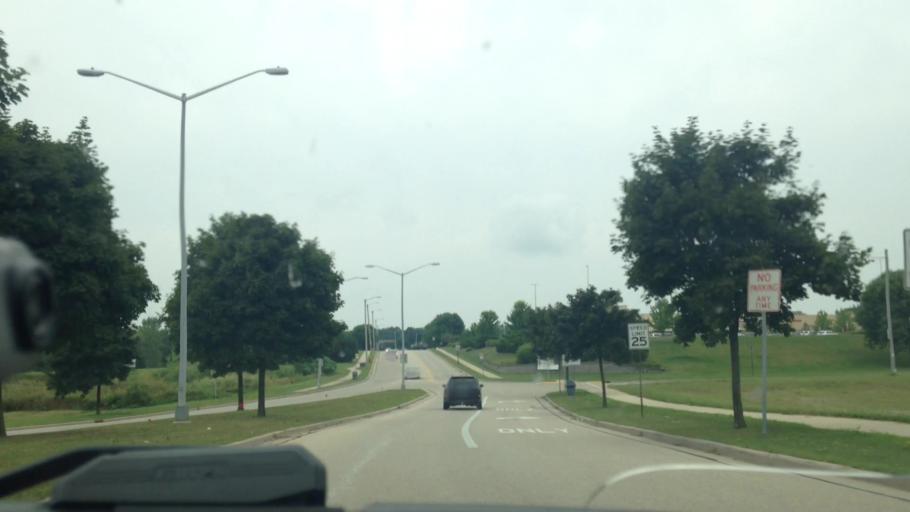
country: US
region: Wisconsin
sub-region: Waukesha County
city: Menomonee Falls
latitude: 43.1919
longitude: -88.1280
